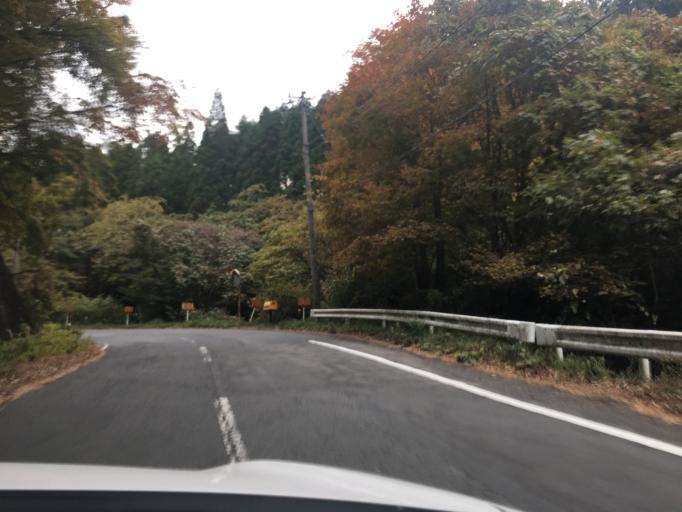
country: JP
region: Fukushima
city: Iwaki
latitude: 37.1232
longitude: 140.7753
